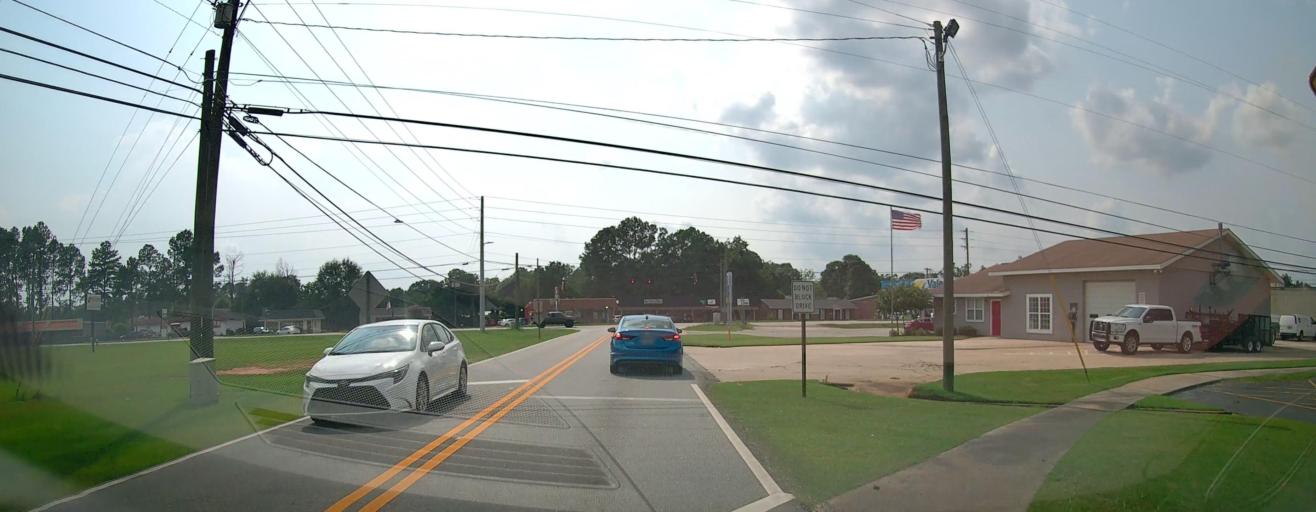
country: US
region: Georgia
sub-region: Houston County
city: Warner Robins
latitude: 32.5783
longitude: -83.6228
